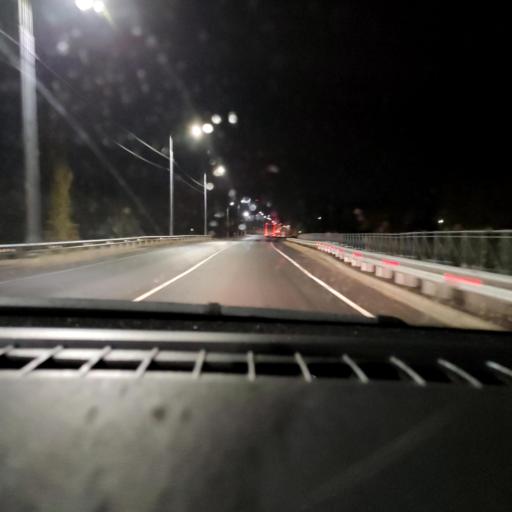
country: RU
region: Voronezj
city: Novaya Usman'
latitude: 51.6260
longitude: 39.3991
